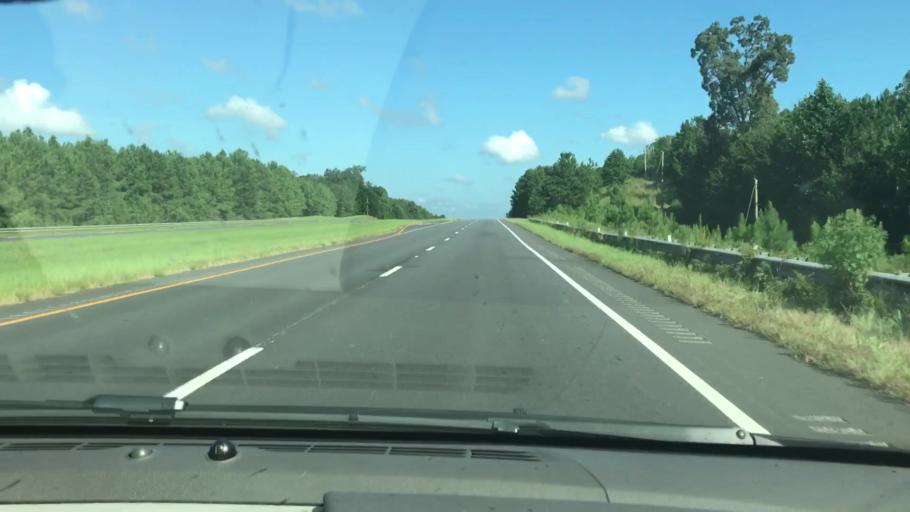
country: US
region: Alabama
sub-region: Barbour County
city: Eufaula
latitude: 32.0445
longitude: -85.1299
